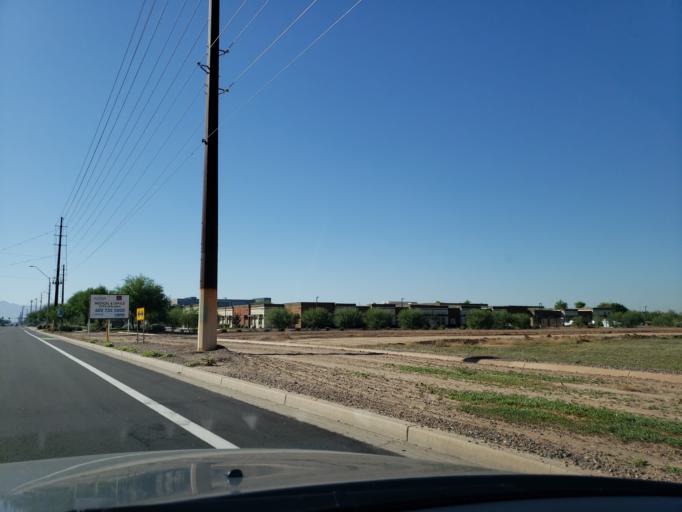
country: US
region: Arizona
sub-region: Maricopa County
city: Tolleson
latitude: 33.4842
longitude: -112.2553
